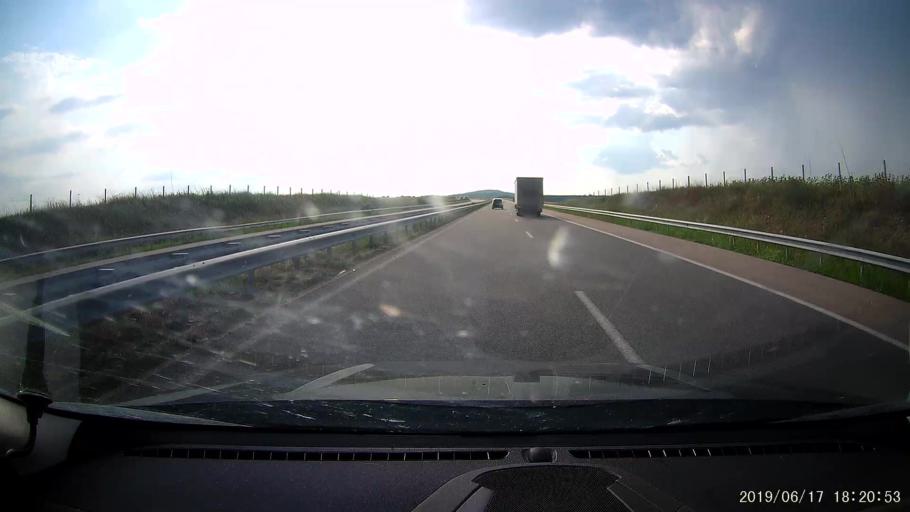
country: BG
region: Khaskovo
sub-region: Obshtina Simeonovgrad
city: Simeonovgrad
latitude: 41.9650
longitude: 25.7996
